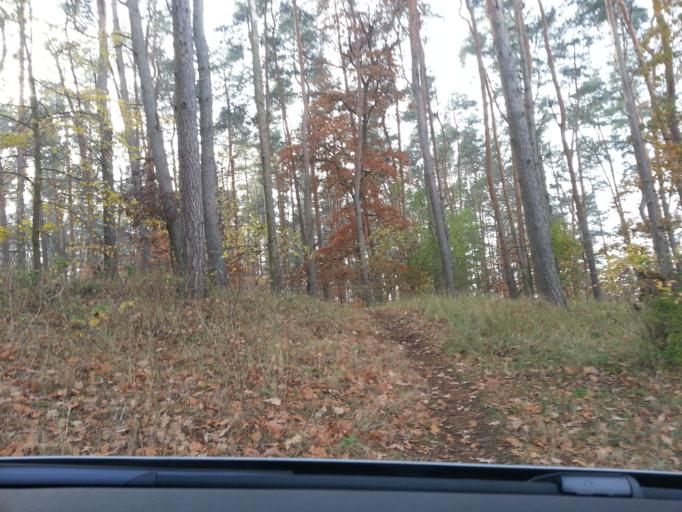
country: DE
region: Mecklenburg-Vorpommern
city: Torgelow
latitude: 53.6261
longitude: 14.0147
